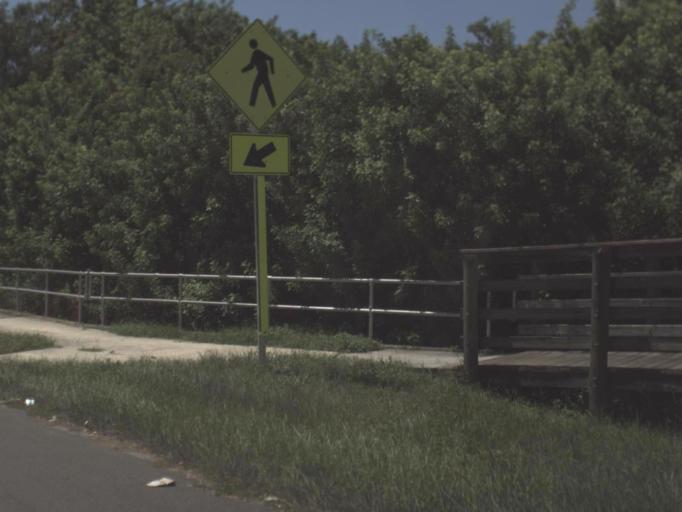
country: US
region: Florida
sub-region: Pinellas County
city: Safety Harbor
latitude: 28.0134
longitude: -82.6841
